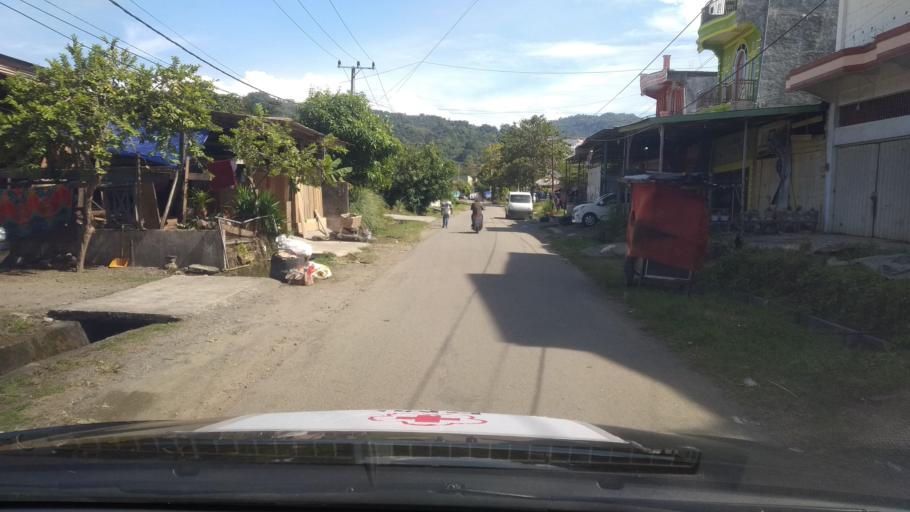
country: ID
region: Sulawesi Barat
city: Mamuju
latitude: -2.6877
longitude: 118.8784
